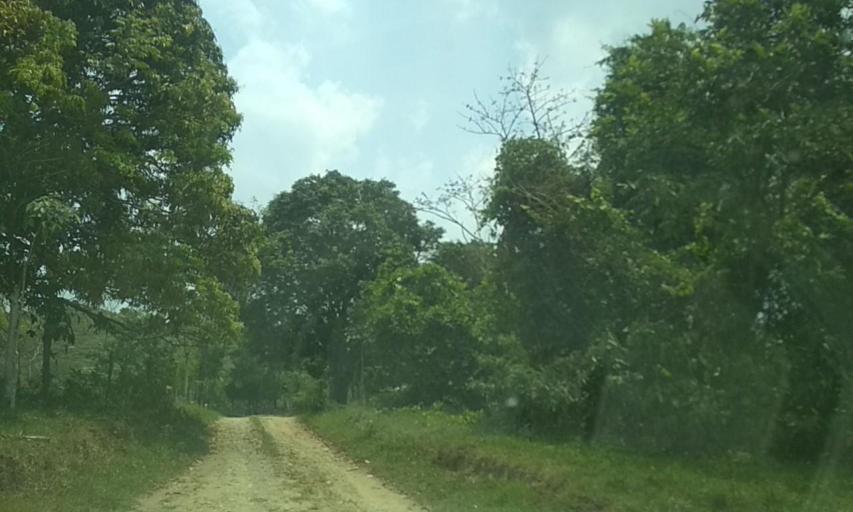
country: MX
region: Tabasco
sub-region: Huimanguillo
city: Francisco Rueda
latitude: 17.5783
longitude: -93.7890
